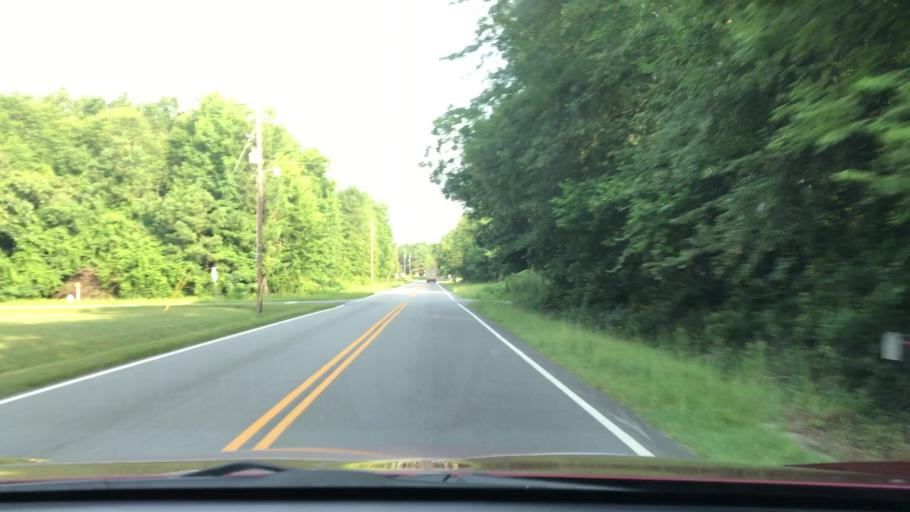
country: US
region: South Carolina
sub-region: Bamberg County
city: Denmark
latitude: 33.5332
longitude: -81.1283
